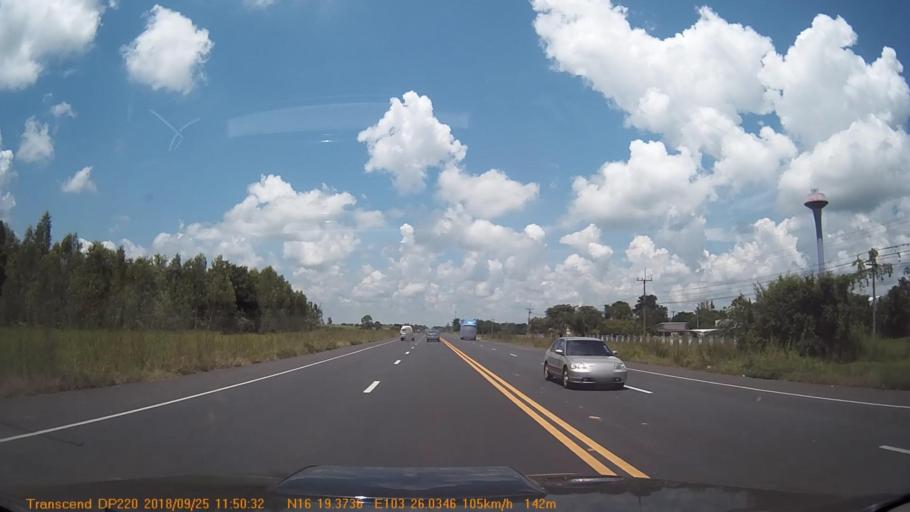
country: TH
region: Kalasin
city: Khong Chai
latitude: 16.3228
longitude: 103.4340
